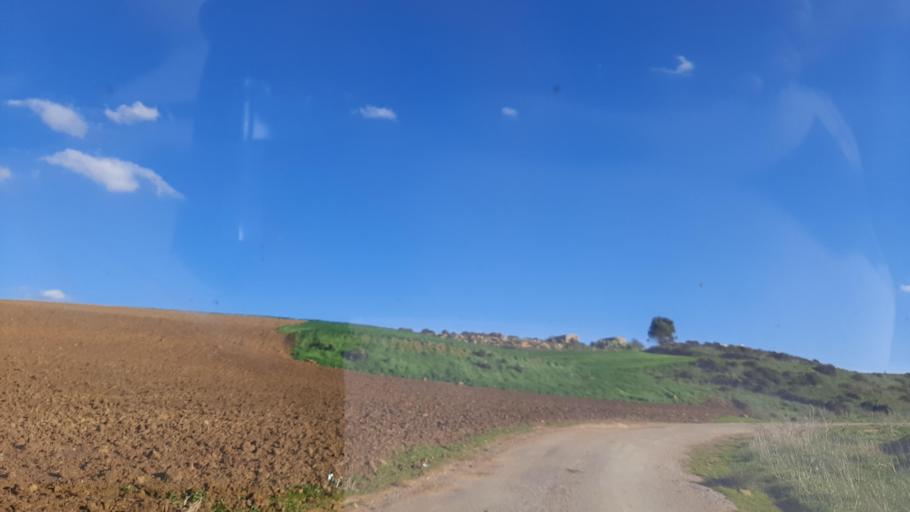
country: TN
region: Nabul
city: El Mida
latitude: 36.8116
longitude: 10.8446
